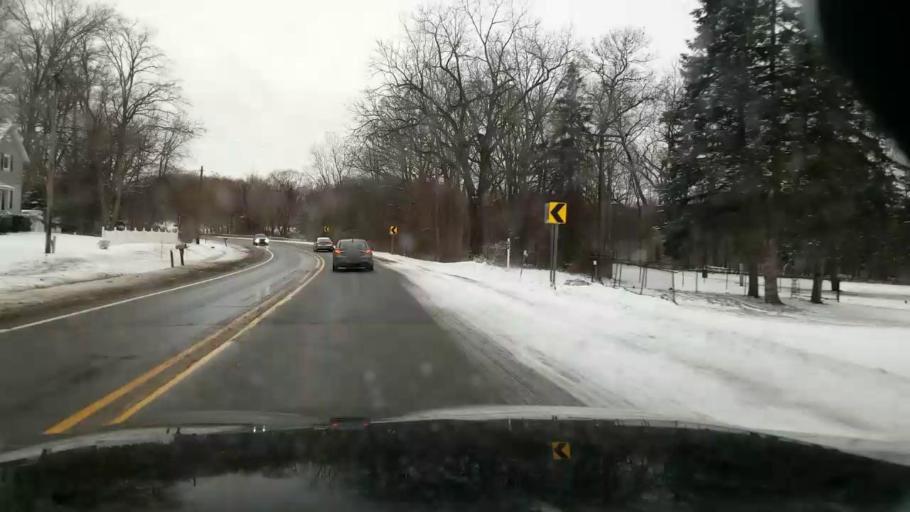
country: US
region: Michigan
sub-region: Jackson County
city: Spring Arbor
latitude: 42.2257
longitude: -84.4914
